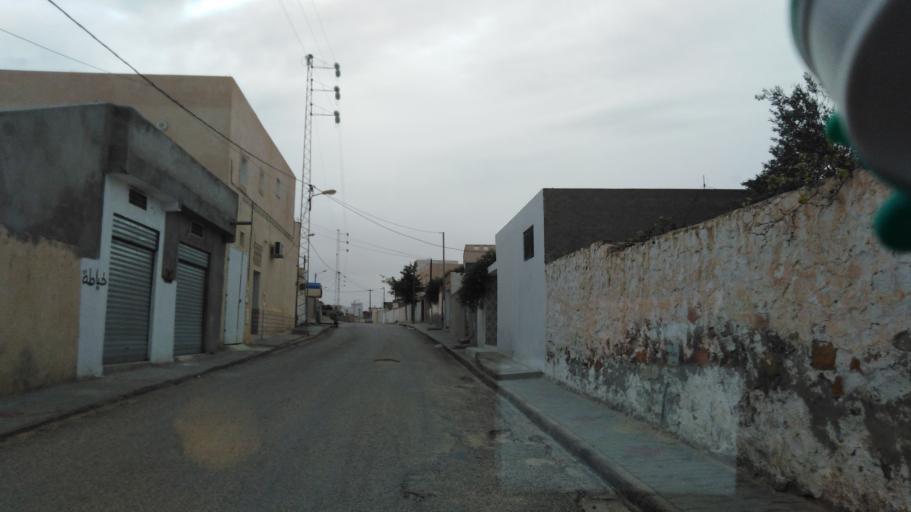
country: TN
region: Qabis
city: Gabes
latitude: 33.9553
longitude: 10.0042
